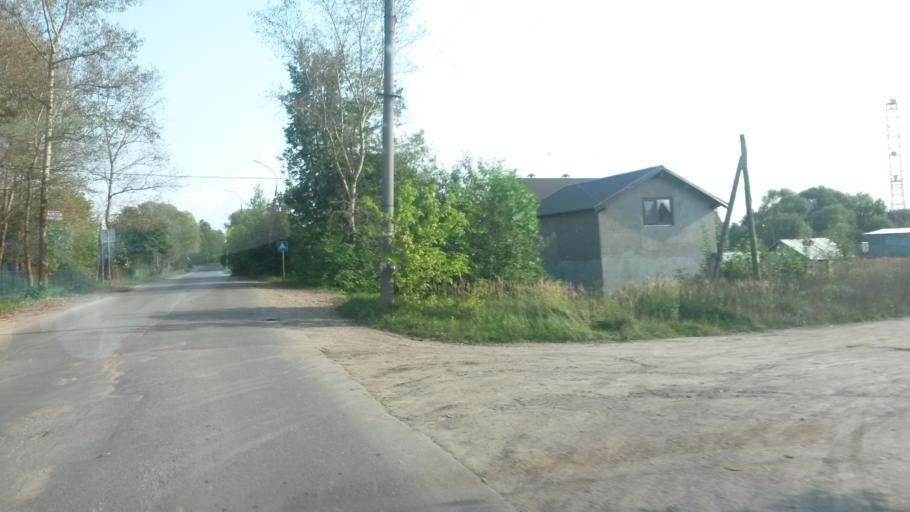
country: RU
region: Jaroslavl
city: Petrovsk
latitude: 57.0084
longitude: 39.2700
